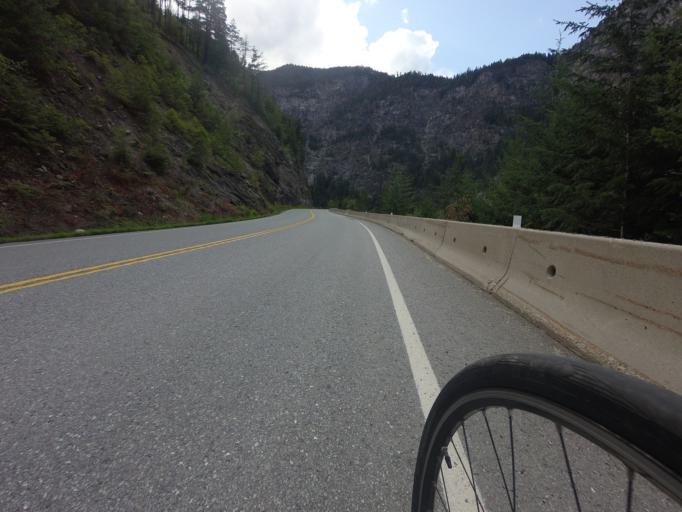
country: CA
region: British Columbia
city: Lillooet
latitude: 50.6458
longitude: -122.0634
